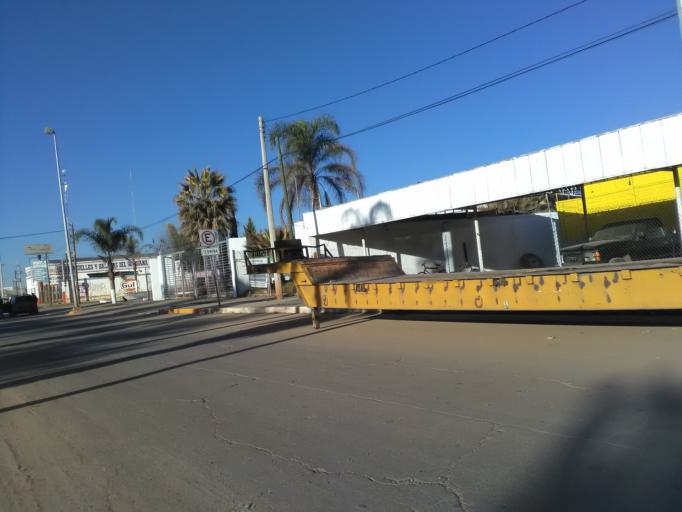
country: MX
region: Durango
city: Victoria de Durango
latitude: 24.0524
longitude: -104.6451
